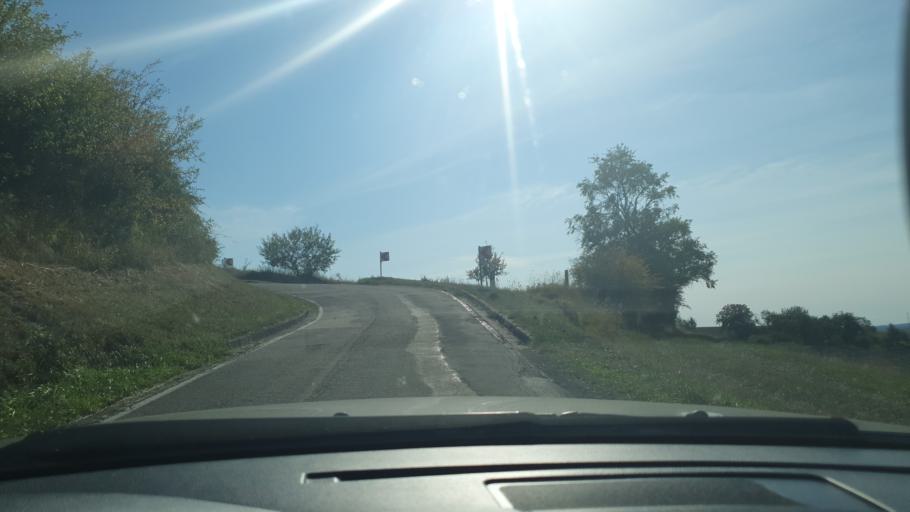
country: DE
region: Rheinland-Pfalz
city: Battweiler
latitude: 49.2875
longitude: 7.4624
